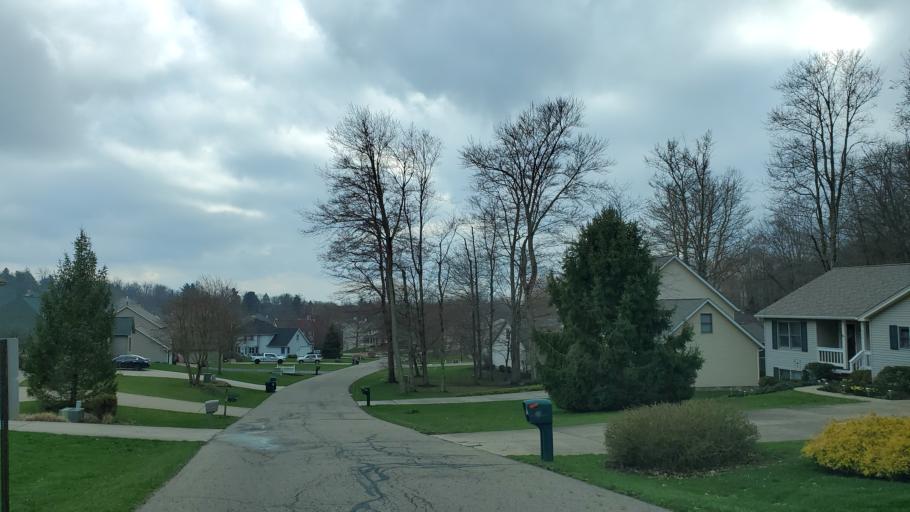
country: US
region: Ohio
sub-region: Licking County
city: Newark
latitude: 40.0358
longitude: -82.3770
